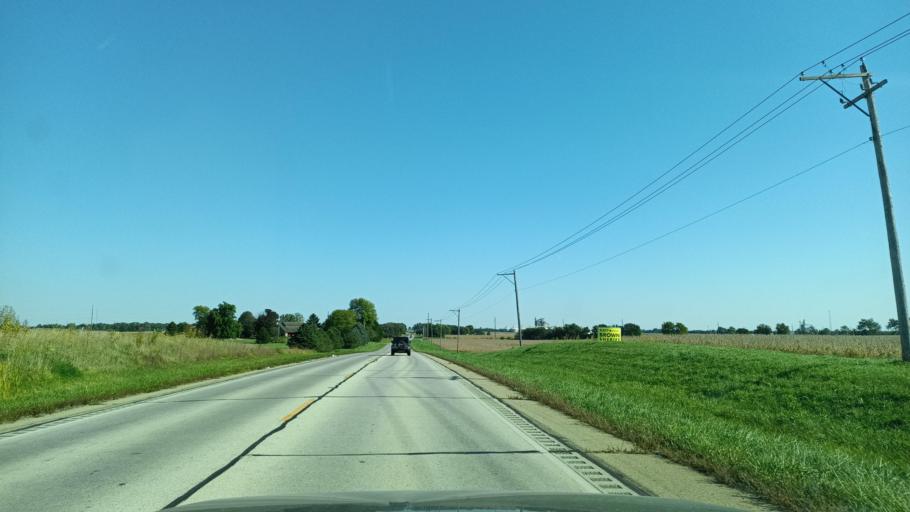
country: US
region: Illinois
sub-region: Champaign County
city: Lake of the Woods
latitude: 40.1749
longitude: -88.3450
